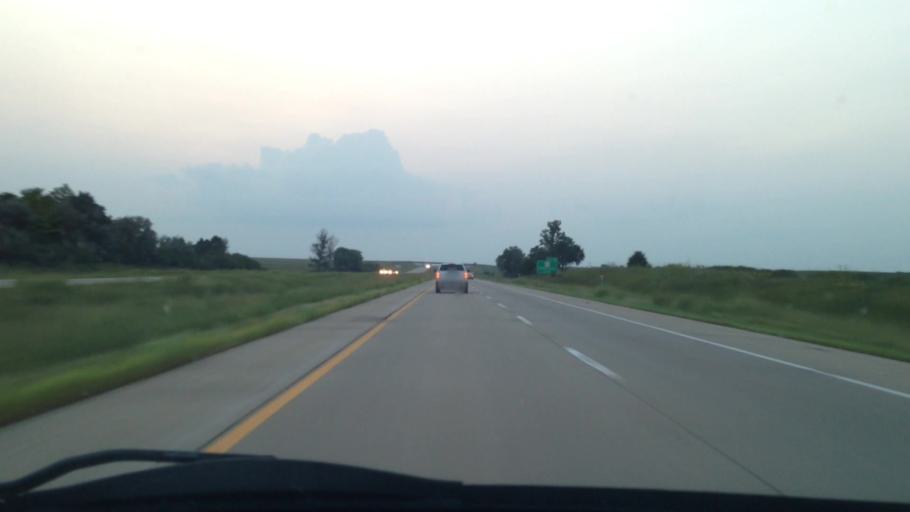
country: US
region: Iowa
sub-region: Black Hawk County
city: La Porte City
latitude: 42.3991
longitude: -92.1493
